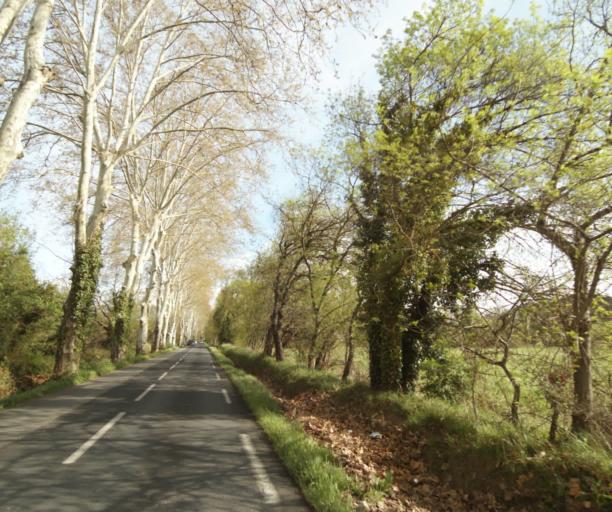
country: FR
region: Languedoc-Roussillon
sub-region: Departement de l'Herault
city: Laverune
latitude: 43.5879
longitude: 3.8186
